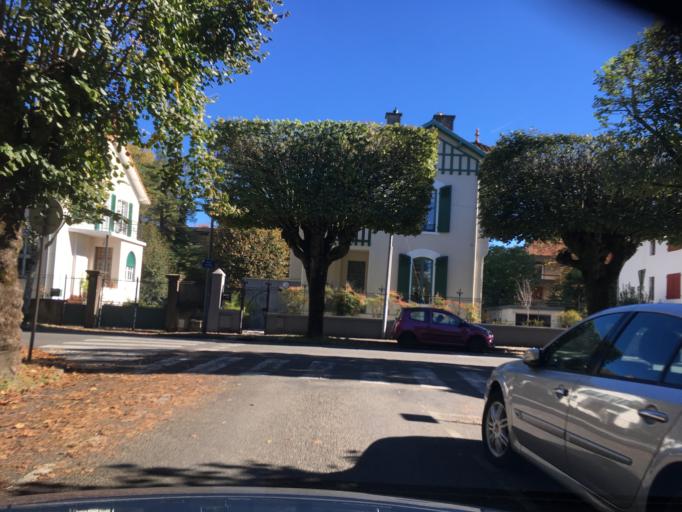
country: FR
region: Aquitaine
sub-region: Departement des Pyrenees-Atlantiques
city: Pau
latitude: 43.2999
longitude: -0.3558
